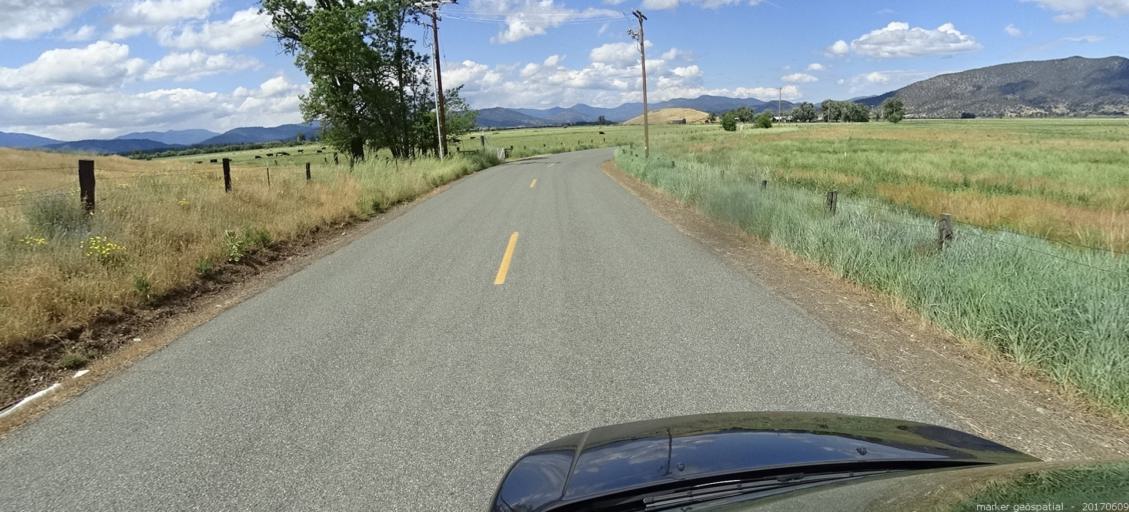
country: US
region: California
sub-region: Siskiyou County
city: Yreka
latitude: 41.4838
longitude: -122.8766
